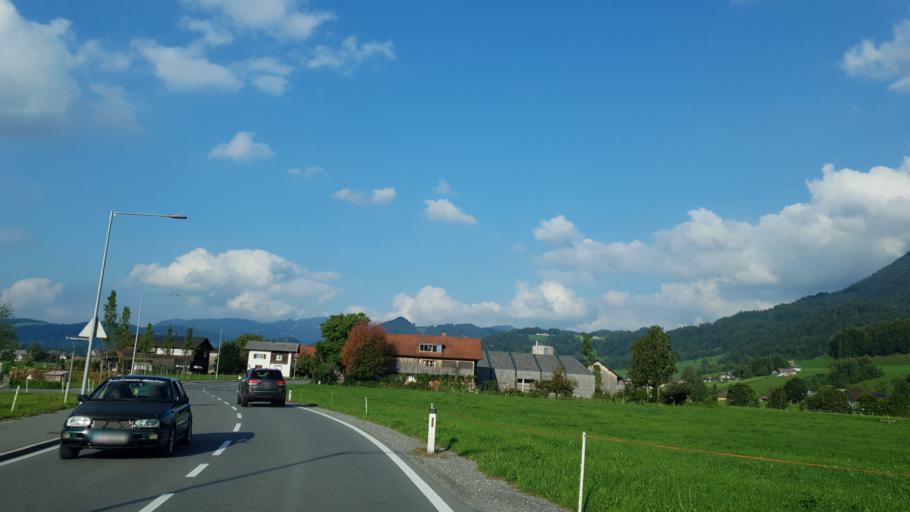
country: AT
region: Vorarlberg
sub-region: Politischer Bezirk Bregenz
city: Andelsbuch
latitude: 47.4057
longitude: 9.8854
